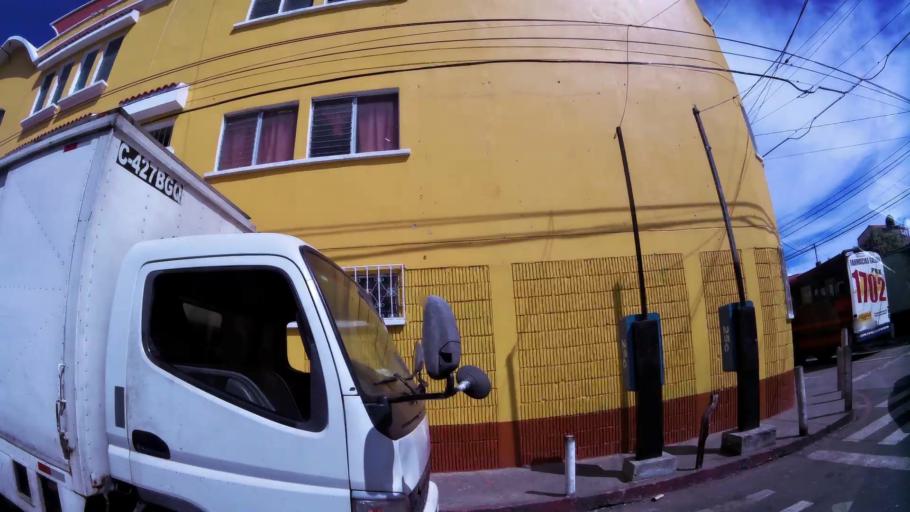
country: GT
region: Guatemala
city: Mixco
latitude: 14.6506
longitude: -90.5825
